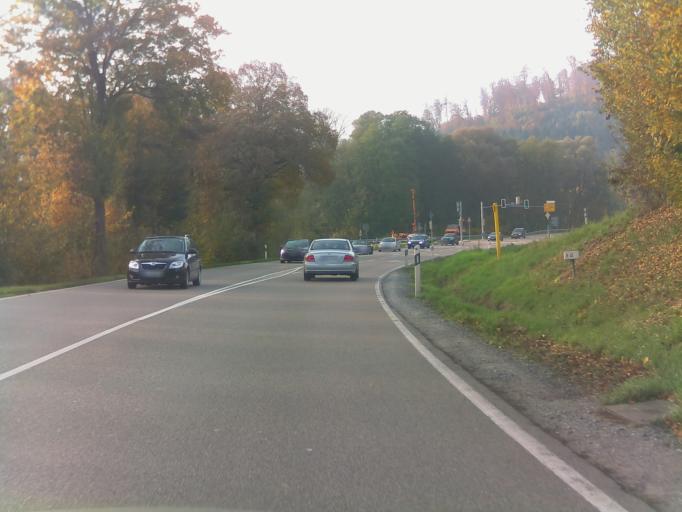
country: DE
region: Baden-Wuerttemberg
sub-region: Karlsruhe Region
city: Wiesenbach
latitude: 49.3603
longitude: 8.7925
